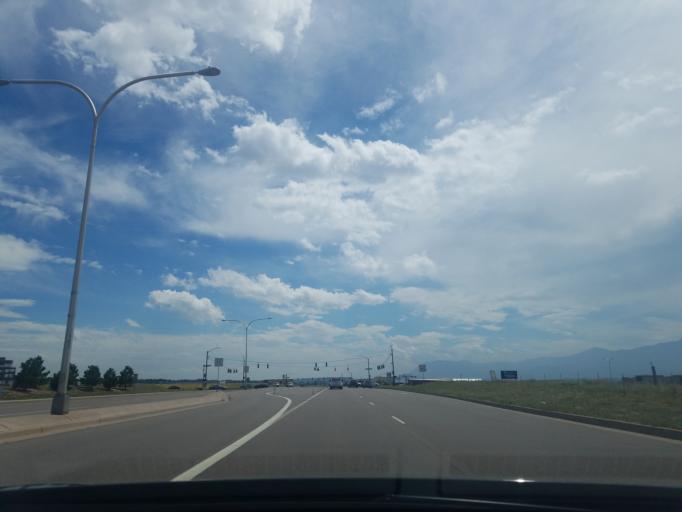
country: US
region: Colorado
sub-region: El Paso County
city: Gleneagle
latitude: 38.9922
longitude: -104.7982
